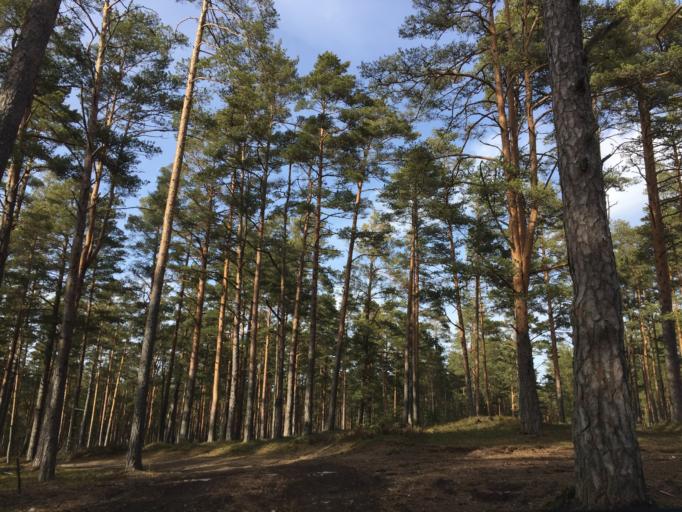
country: EE
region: Paernumaa
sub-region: Paernu linn
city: Parnu
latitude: 58.2280
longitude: 24.5143
